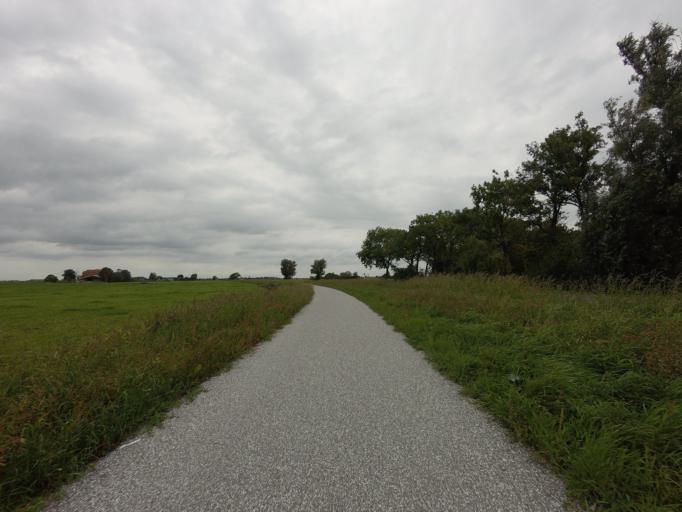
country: NL
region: Friesland
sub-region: Sudwest Fryslan
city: IJlst
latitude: 53.0450
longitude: 5.6126
